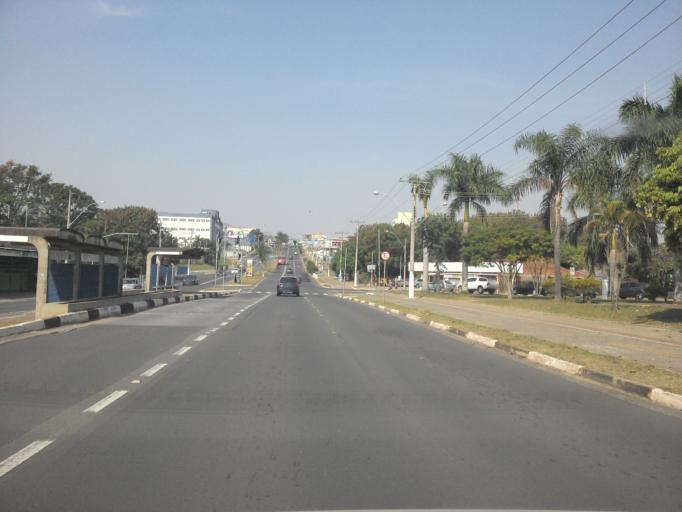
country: BR
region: Sao Paulo
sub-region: Hortolandia
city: Hortolandia
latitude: -22.8693
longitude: -47.2212
